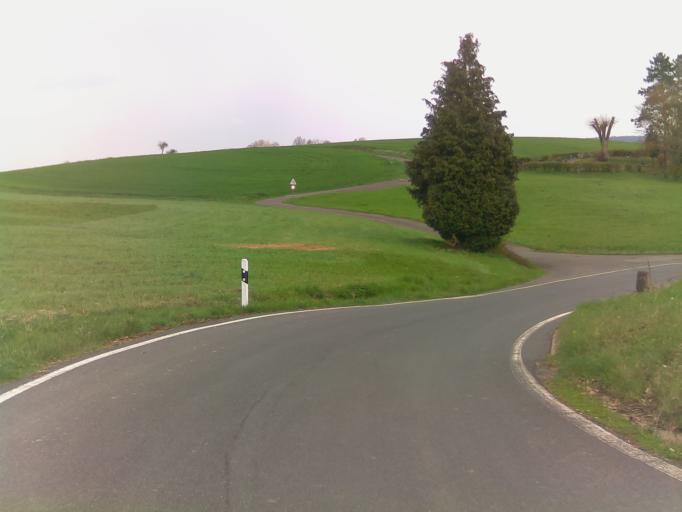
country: DE
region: Rheinland-Pfalz
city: Daubach
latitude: 49.8570
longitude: 7.6380
